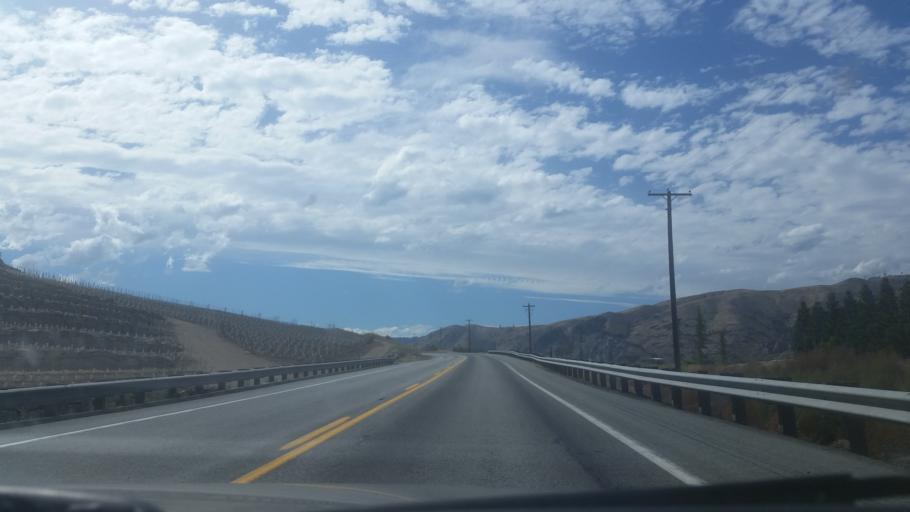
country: US
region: Washington
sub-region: Chelan County
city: Chelan
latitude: 47.7676
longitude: -120.1107
